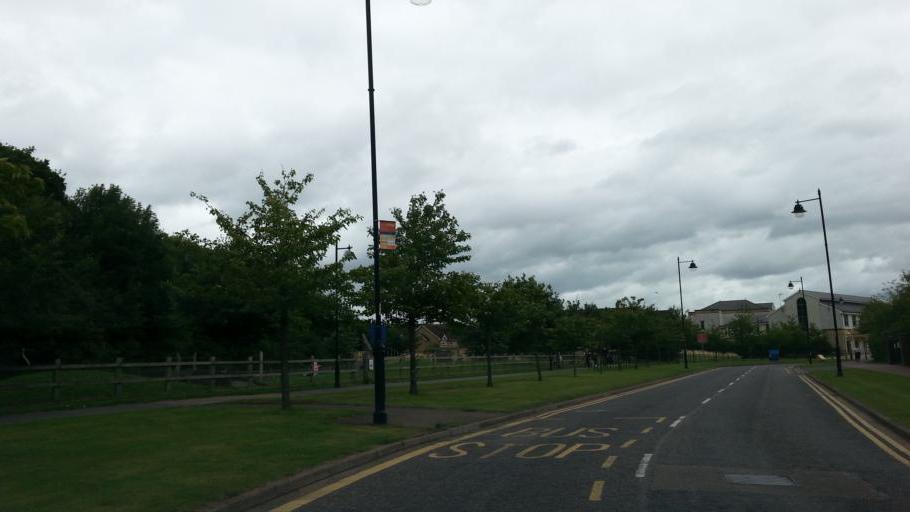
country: GB
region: England
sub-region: Cambridgeshire
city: Papworth Everard
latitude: 52.2174
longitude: -0.0724
